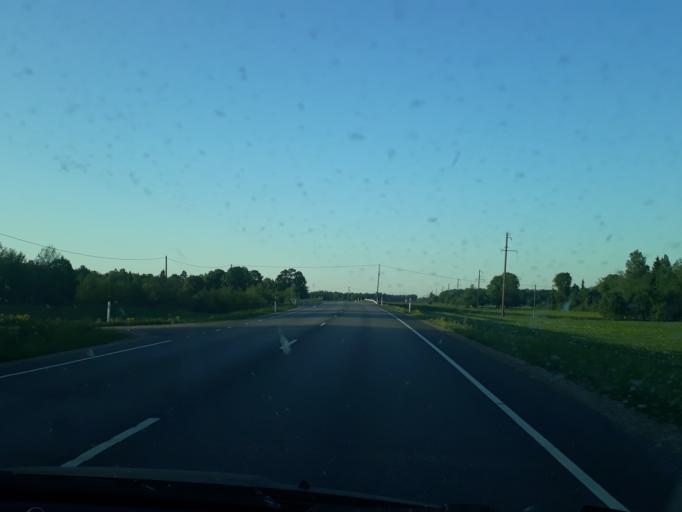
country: EE
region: Paernumaa
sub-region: Tootsi vald
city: Tootsi
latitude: 58.5636
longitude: 24.8707
